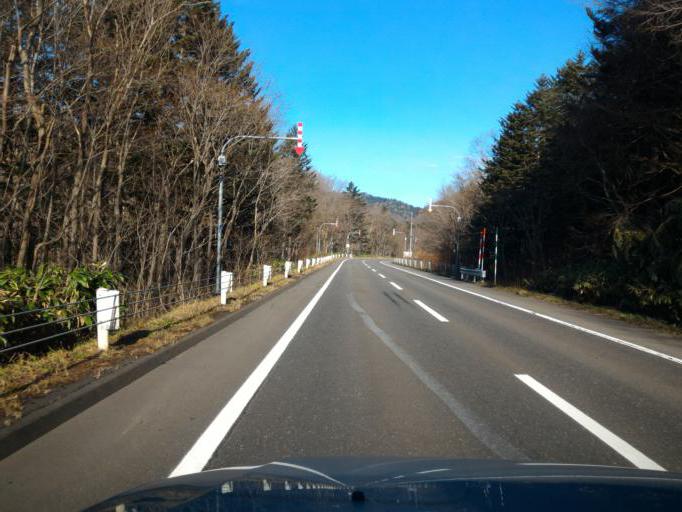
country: JP
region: Hokkaido
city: Ashibetsu
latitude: 43.3362
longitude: 142.1523
